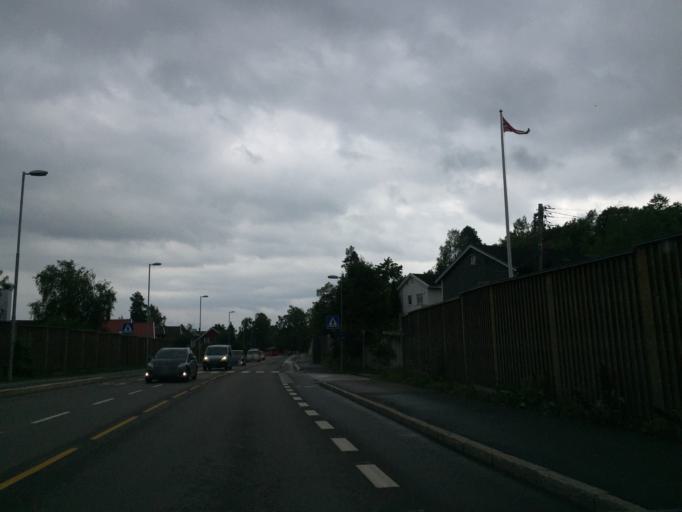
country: NO
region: Oslo
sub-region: Oslo
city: Sjolyststranda
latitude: 59.9492
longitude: 10.6761
